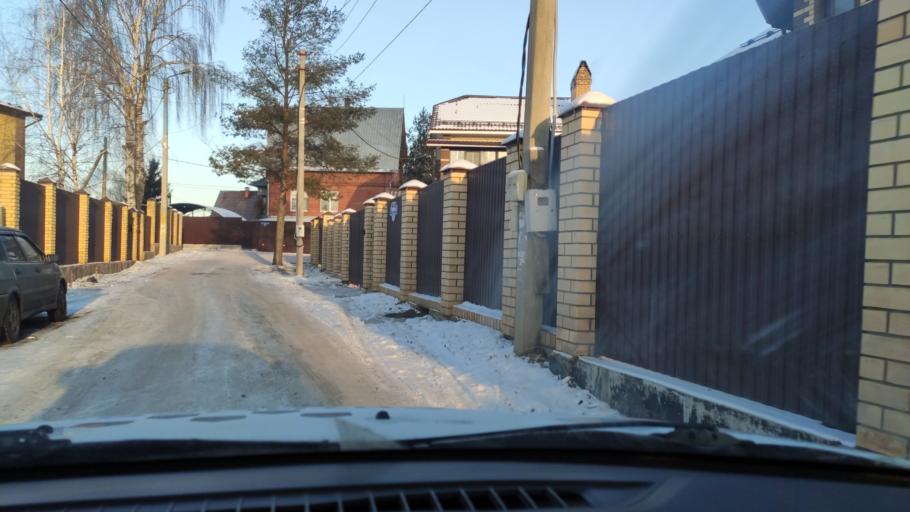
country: RU
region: Perm
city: Perm
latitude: 58.0313
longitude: 56.2288
